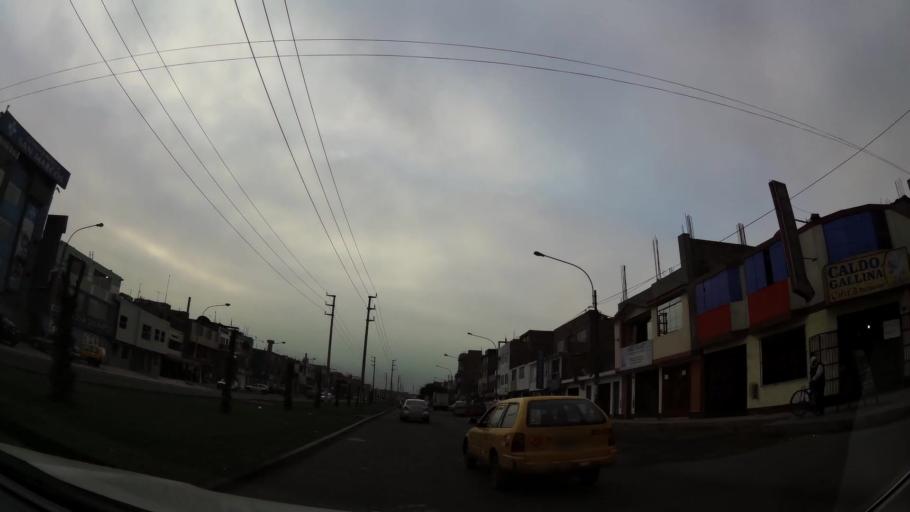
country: PE
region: Lima
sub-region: Lima
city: Independencia
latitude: -12.0020
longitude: -76.9992
